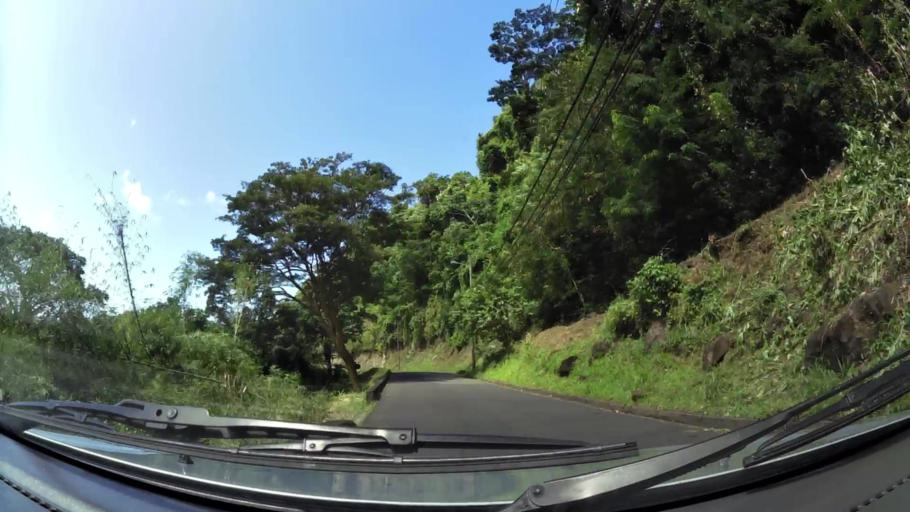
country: GD
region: Saint John
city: Gouyave
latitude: 12.1192
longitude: -61.7396
